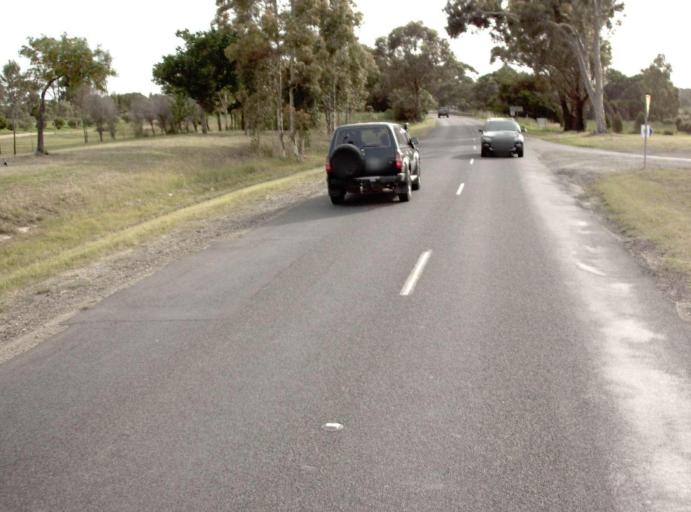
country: AU
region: Victoria
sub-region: Latrobe
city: Traralgon
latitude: -38.0614
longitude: 146.6226
